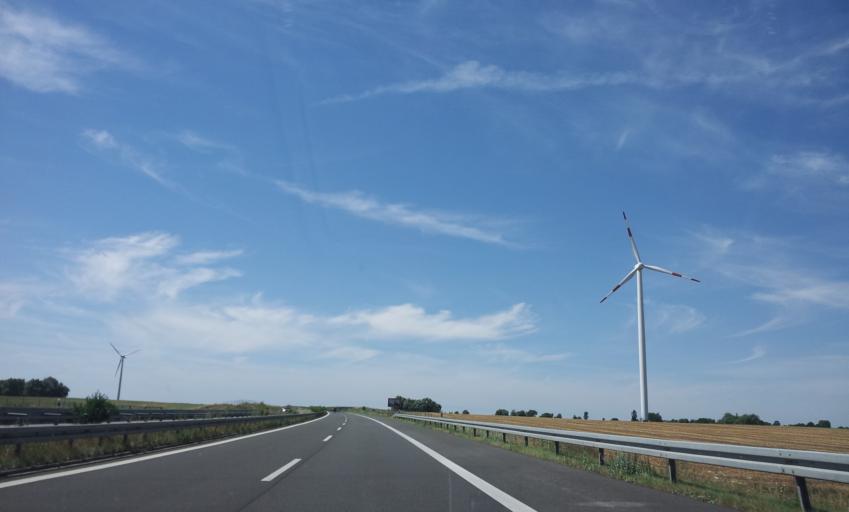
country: DE
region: Mecklenburg-Vorpommern
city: Strasburg
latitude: 53.5196
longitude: 13.8180
